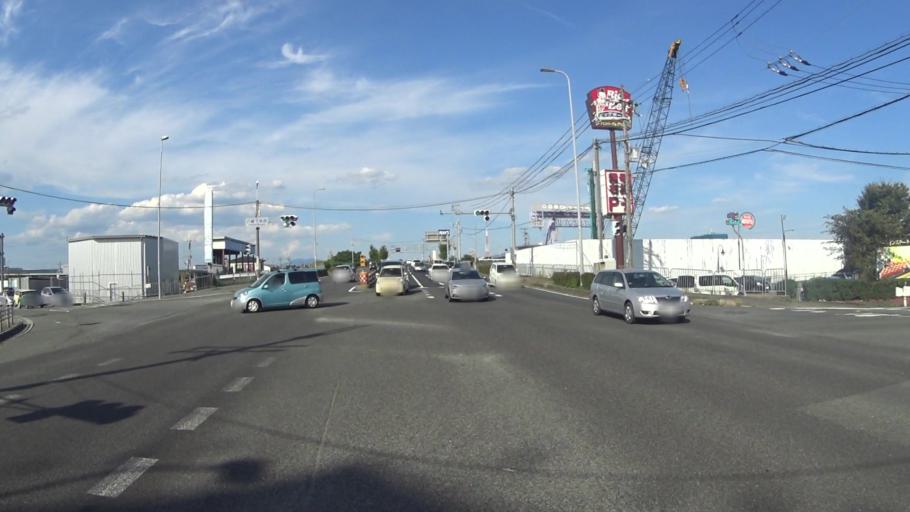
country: JP
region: Kyoto
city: Yawata
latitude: 34.8710
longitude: 135.7295
